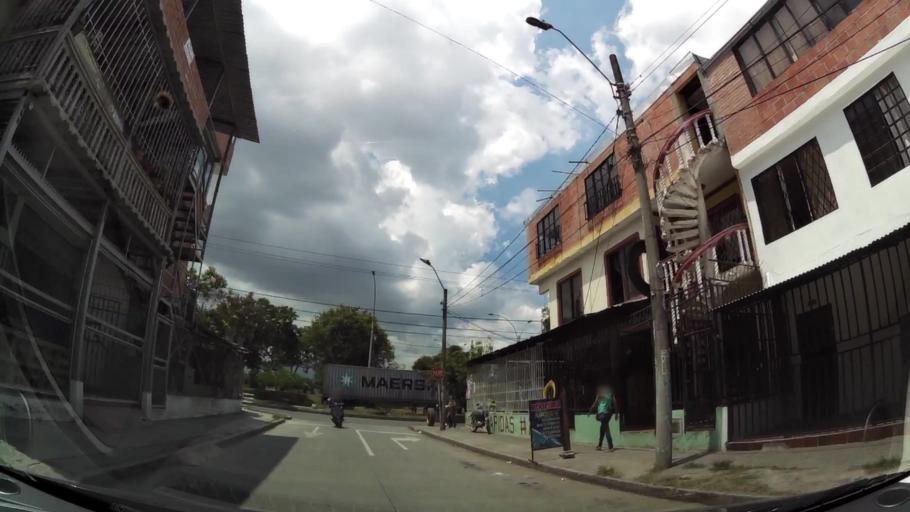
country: CO
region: Valle del Cauca
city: Cali
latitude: 3.4711
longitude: -76.4855
